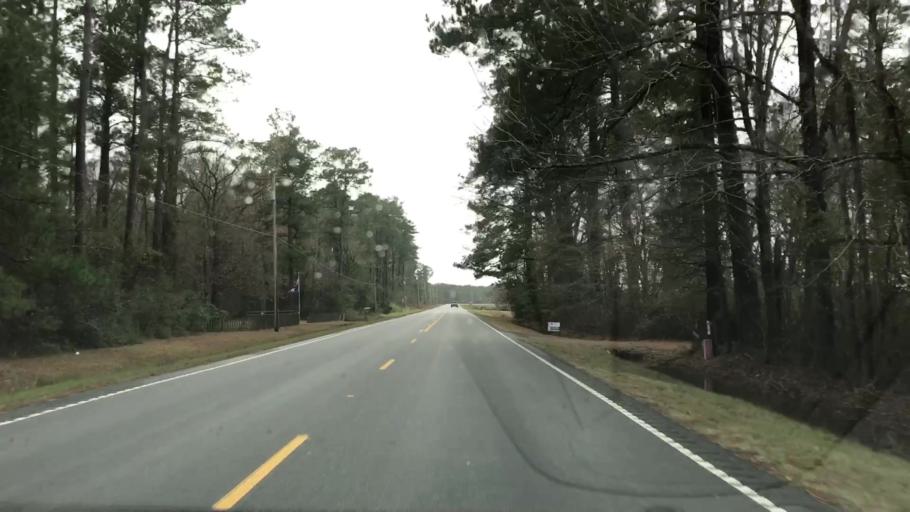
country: US
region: South Carolina
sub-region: Horry County
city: Socastee
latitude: 33.7293
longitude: -79.0838
